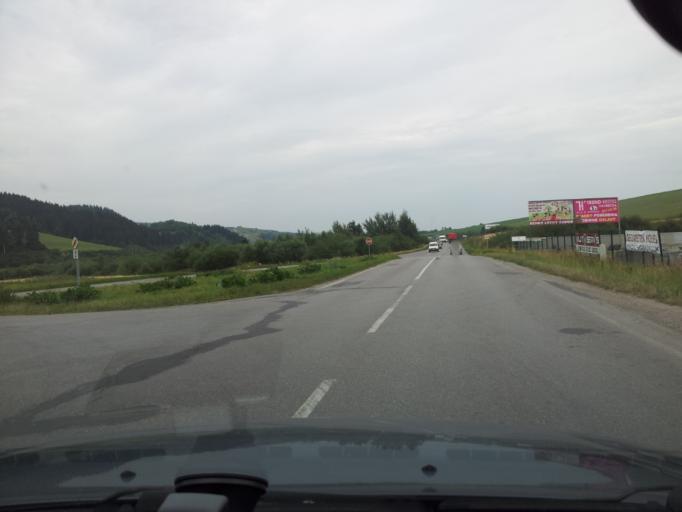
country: SK
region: Zilinsky
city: Namestovo
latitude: 49.3707
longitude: 19.4176
